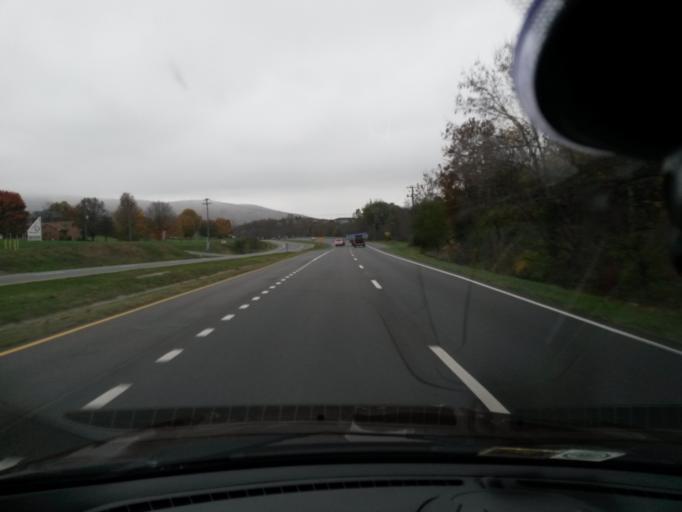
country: US
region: Virginia
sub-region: Botetourt County
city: Laymantown
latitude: 37.3390
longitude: -79.8758
